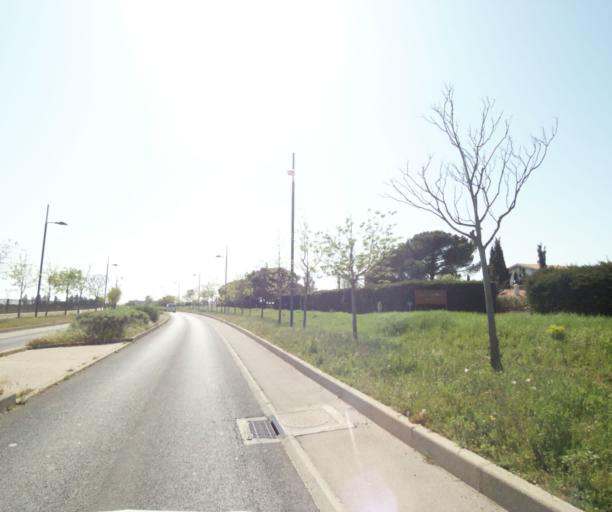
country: FR
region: Languedoc-Roussillon
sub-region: Departement de l'Herault
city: Castelnau-le-Lez
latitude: 43.6243
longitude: 3.9198
